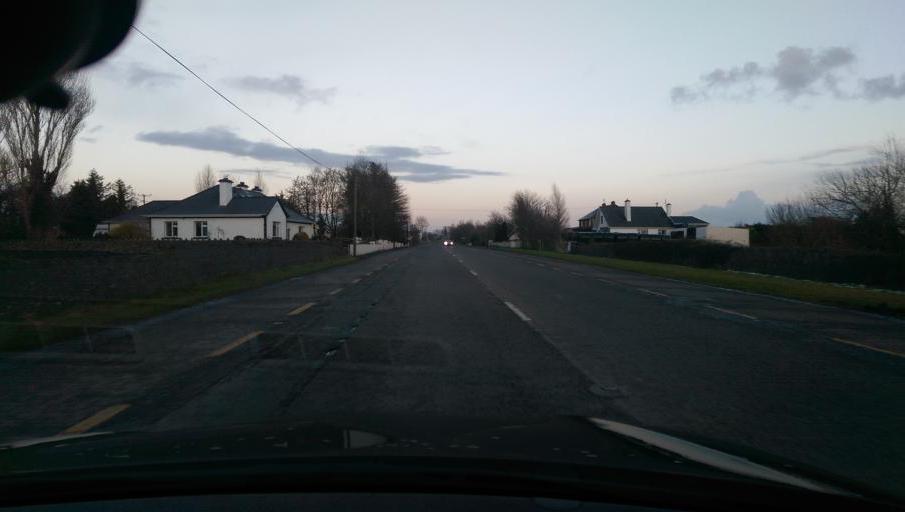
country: IE
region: Connaught
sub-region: County Galway
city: Ballinasloe
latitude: 53.3286
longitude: -8.1810
